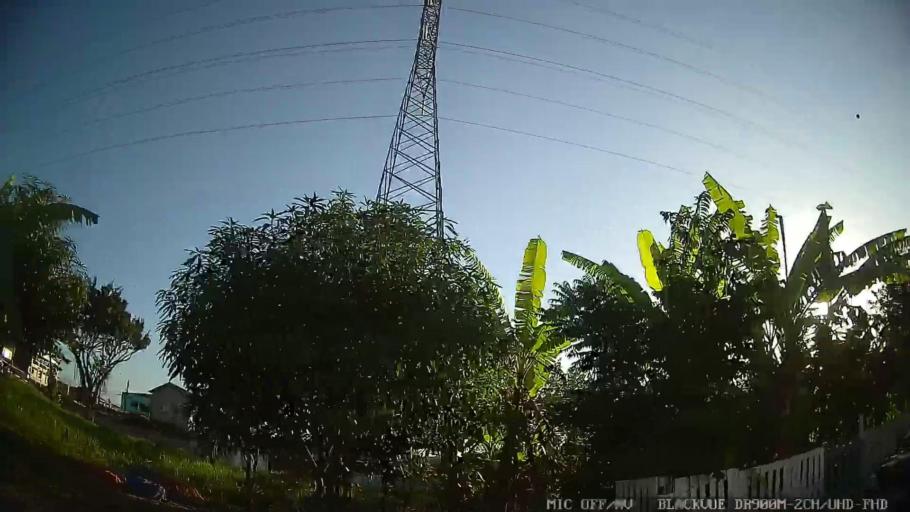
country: BR
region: Sao Paulo
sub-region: Guaruja
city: Guaruja
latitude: -23.9713
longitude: -46.2741
